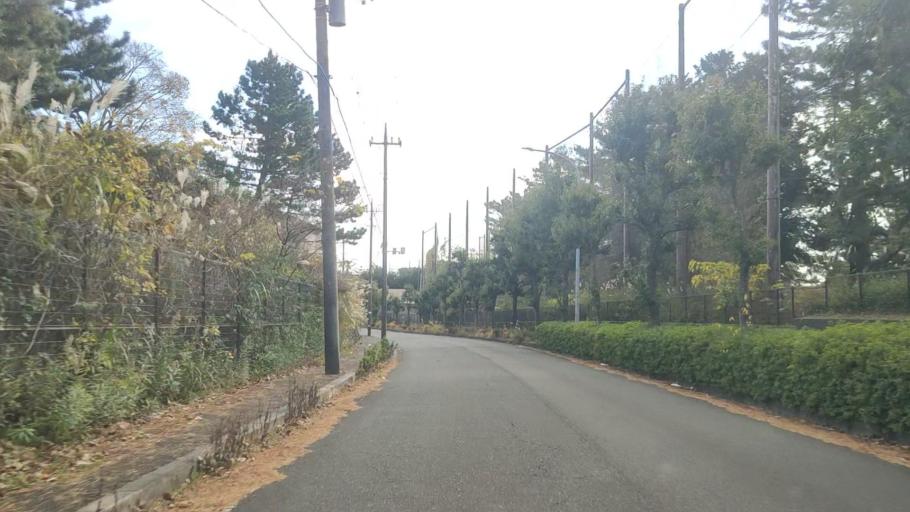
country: JP
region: Kanagawa
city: Yokohama
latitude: 35.4487
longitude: 139.5456
